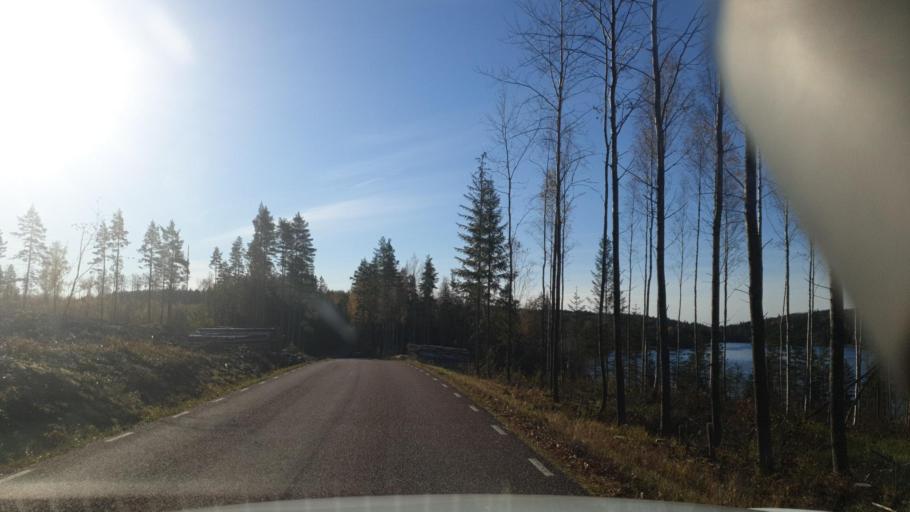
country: SE
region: Vaermland
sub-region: Grums Kommun
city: Grums
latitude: 59.4239
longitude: 13.0867
